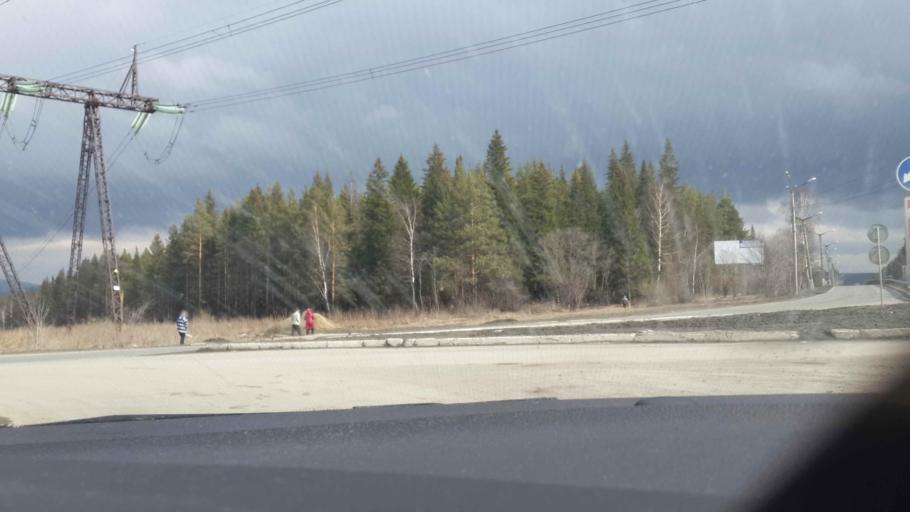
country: RU
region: Chelyabinsk
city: Zlatoust
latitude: 55.1364
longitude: 59.6726
